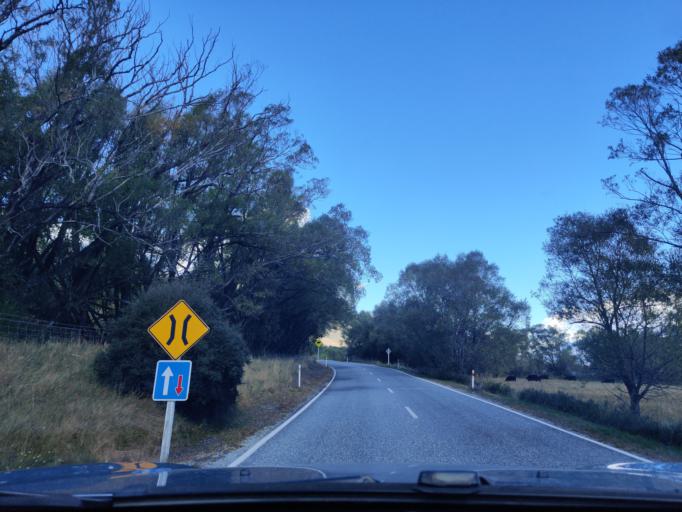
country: NZ
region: Otago
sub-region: Queenstown-Lakes District
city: Queenstown
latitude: -44.7851
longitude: 168.3952
